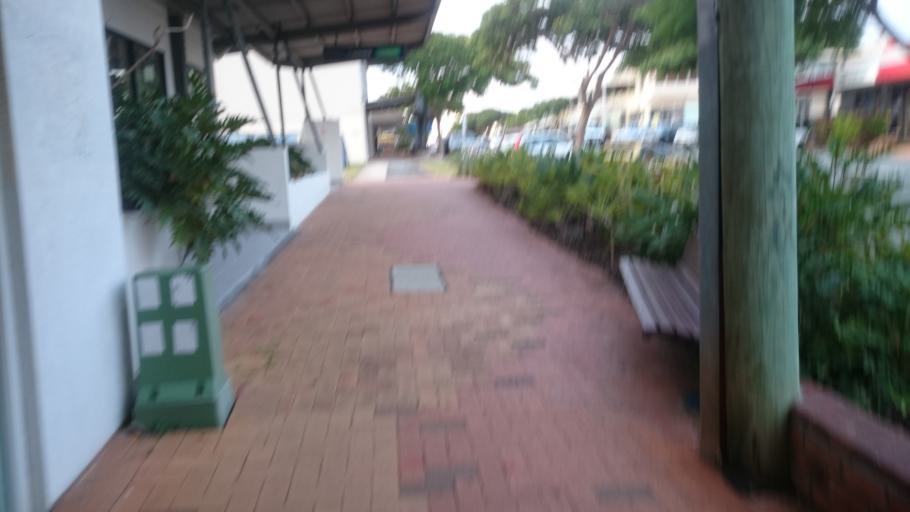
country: AU
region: Queensland
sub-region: Redland
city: Cleveland
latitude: -27.5294
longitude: 153.2670
